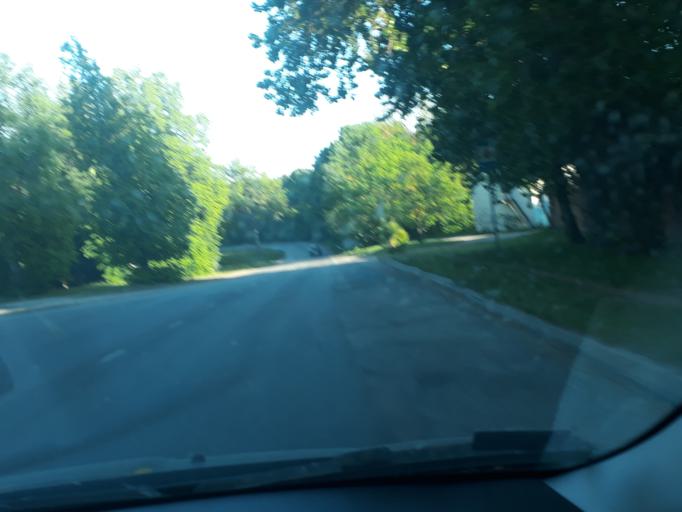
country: EE
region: Paernumaa
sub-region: Paernu linn
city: Parnu
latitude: 58.3875
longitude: 24.5316
